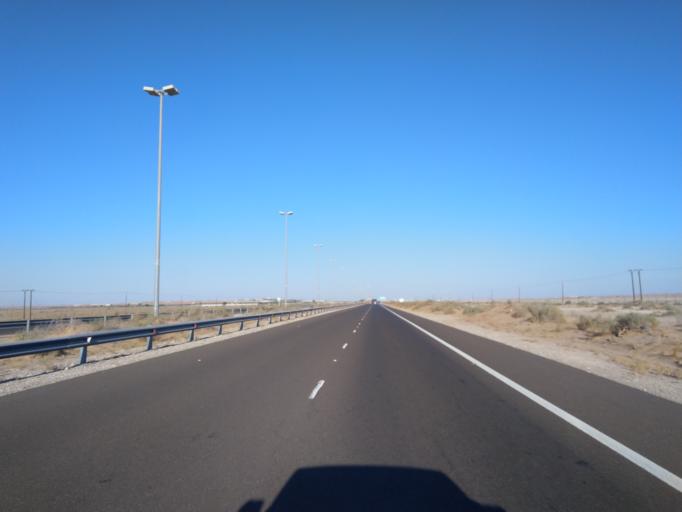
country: OM
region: Al Buraimi
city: Al Buraymi
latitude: 24.4987
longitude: 55.4367
